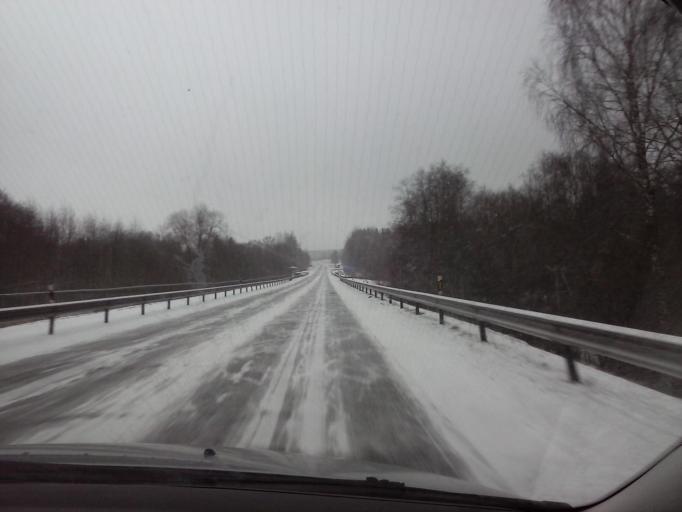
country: EE
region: Valgamaa
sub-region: Valga linn
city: Valga
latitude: 57.8525
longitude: 26.1346
